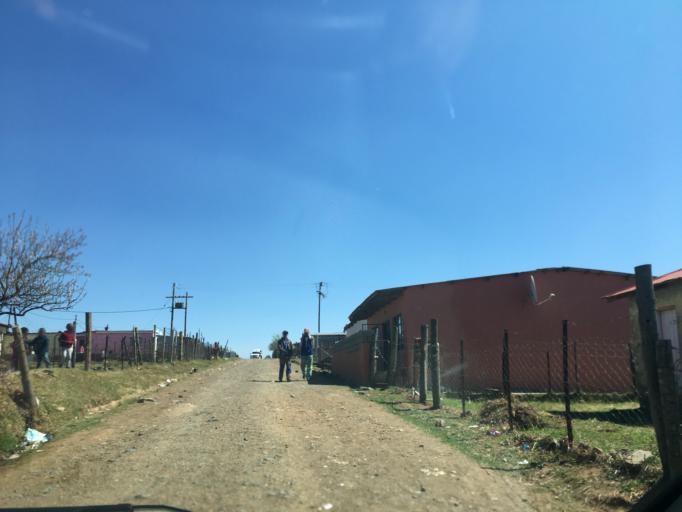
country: ZA
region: Eastern Cape
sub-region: Chris Hani District Municipality
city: Elliot
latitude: -31.3310
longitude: 27.8245
